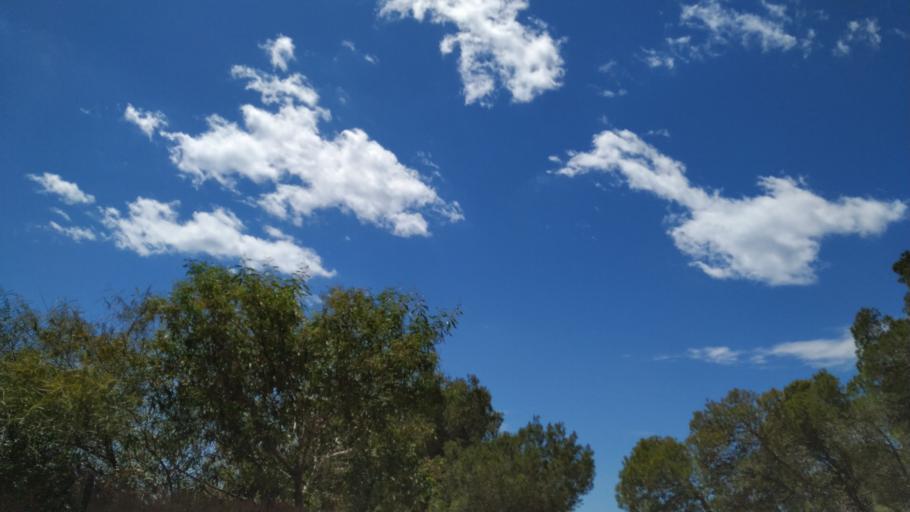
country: ES
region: Balearic Islands
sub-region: Illes Balears
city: Ibiza
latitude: 38.9213
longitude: 1.4749
